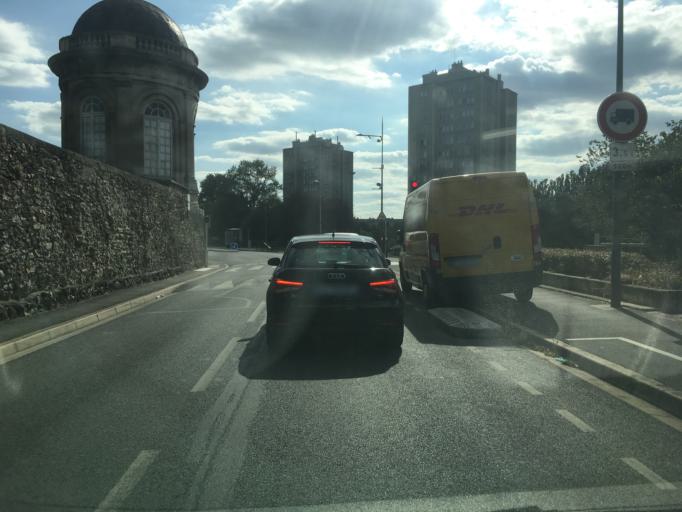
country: FR
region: Ile-de-France
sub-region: Departement du Val-de-Marne
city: Valenton
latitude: 48.7448
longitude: 2.4597
